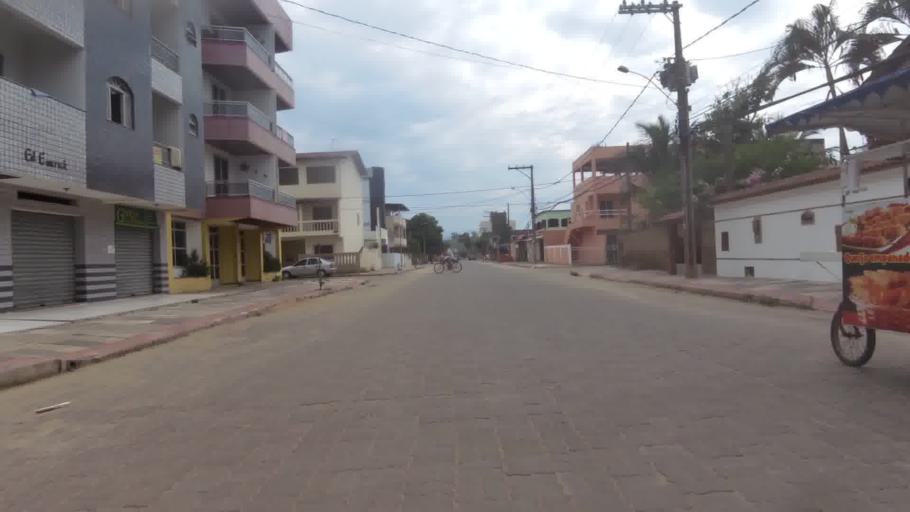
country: BR
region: Espirito Santo
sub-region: Piuma
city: Piuma
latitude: -20.8448
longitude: -40.7420
